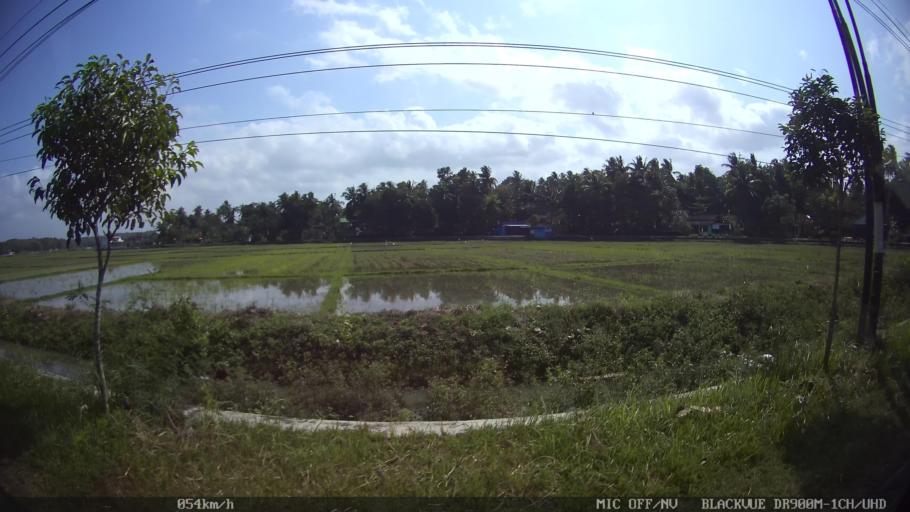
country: ID
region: Daerah Istimewa Yogyakarta
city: Srandakan
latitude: -7.9337
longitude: 110.2155
